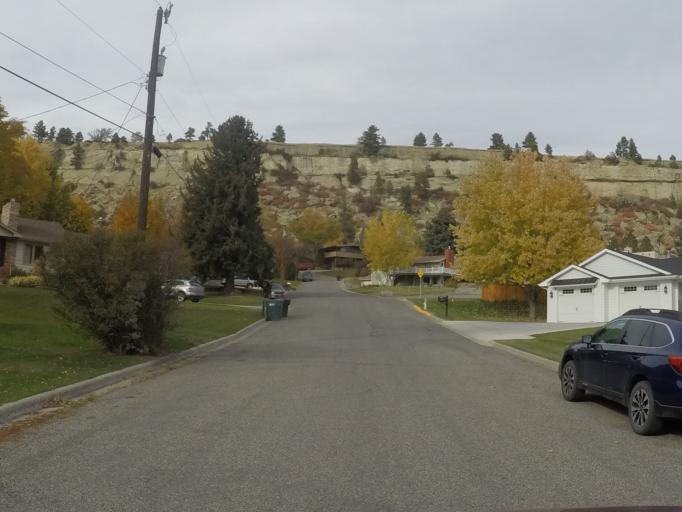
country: US
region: Montana
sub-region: Yellowstone County
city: Billings
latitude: 45.7998
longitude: -108.5487
